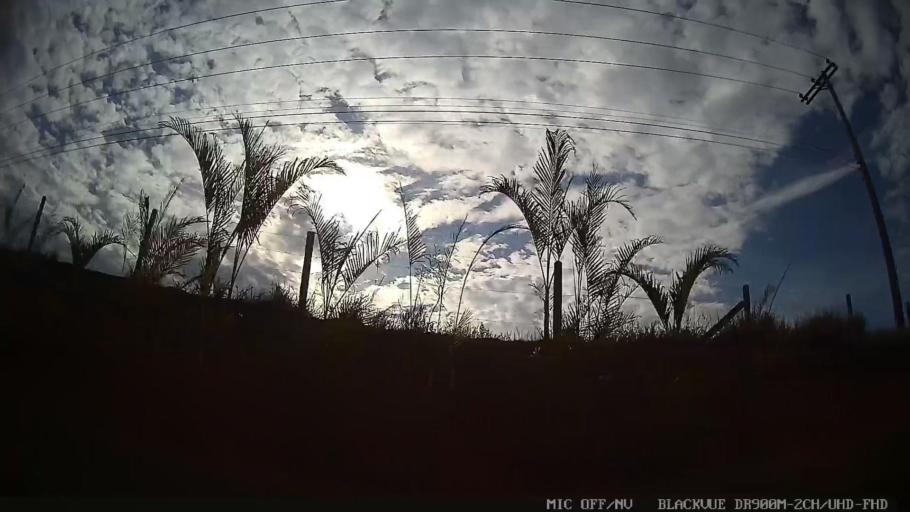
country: BR
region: Sao Paulo
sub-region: Salto
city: Salto
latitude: -23.1784
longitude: -47.2736
